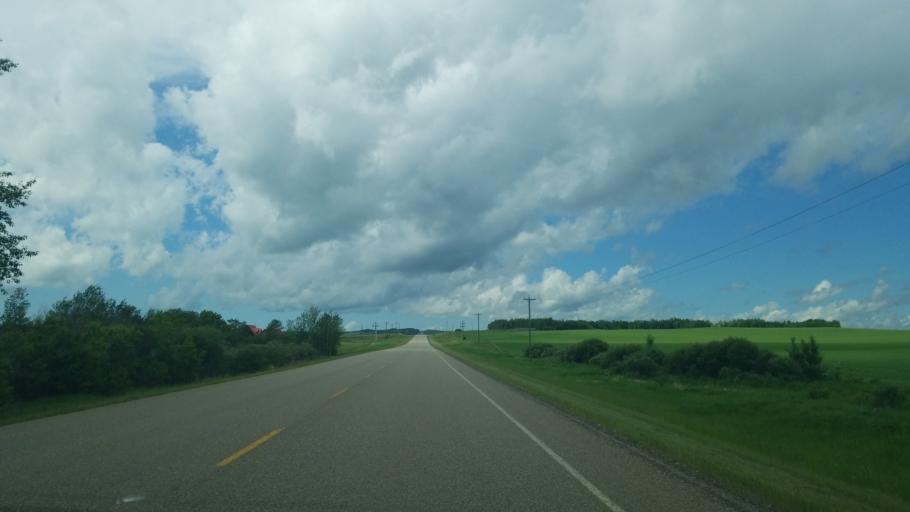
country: CA
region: Saskatchewan
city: Lloydminster
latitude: 53.1617
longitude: -110.1675
